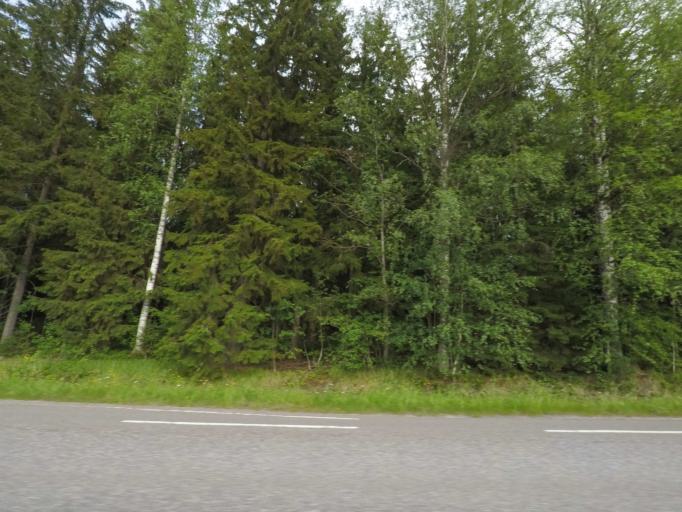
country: FI
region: Paijanne Tavastia
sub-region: Lahti
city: Hollola
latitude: 60.8460
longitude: 25.4950
